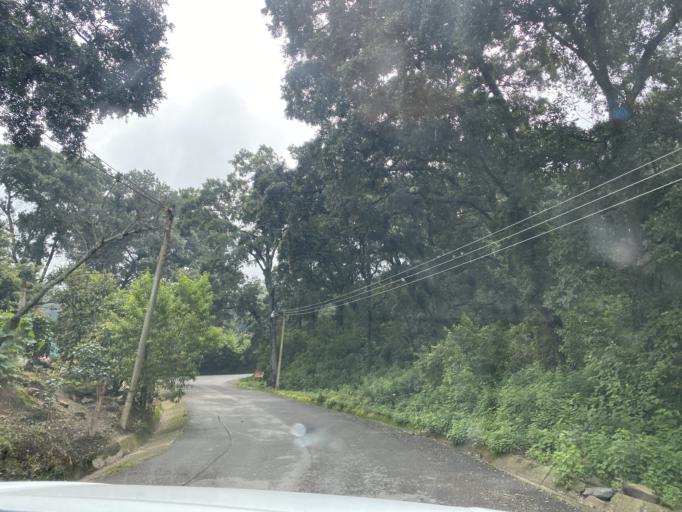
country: MX
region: Morelos
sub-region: Yecapixtla
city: Achichipico
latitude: 18.9412
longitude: -98.8251
